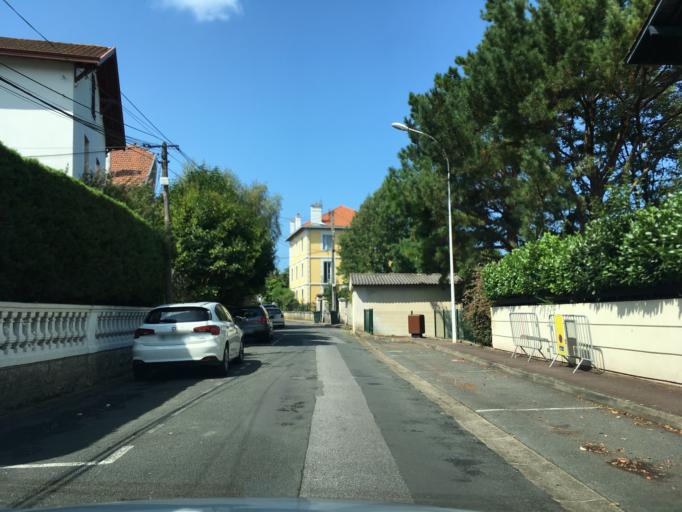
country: FR
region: Aquitaine
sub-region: Departement des Pyrenees-Atlantiques
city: Bayonne
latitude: 43.4955
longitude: -1.4881
